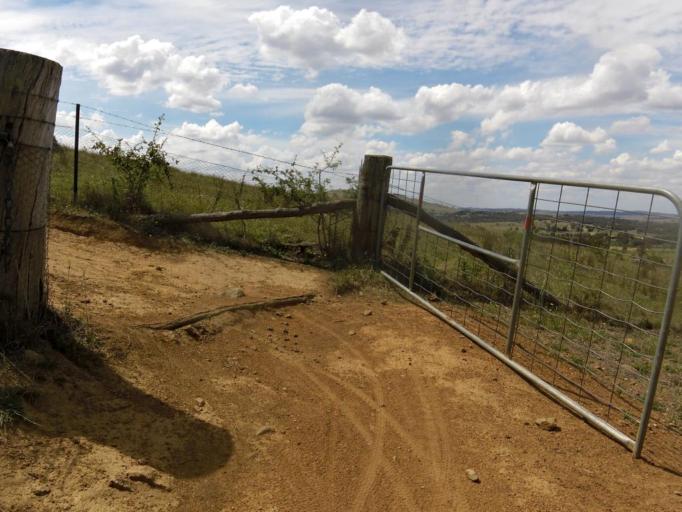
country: AU
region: Australian Capital Territory
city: Belconnen
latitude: -35.1384
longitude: 149.0947
